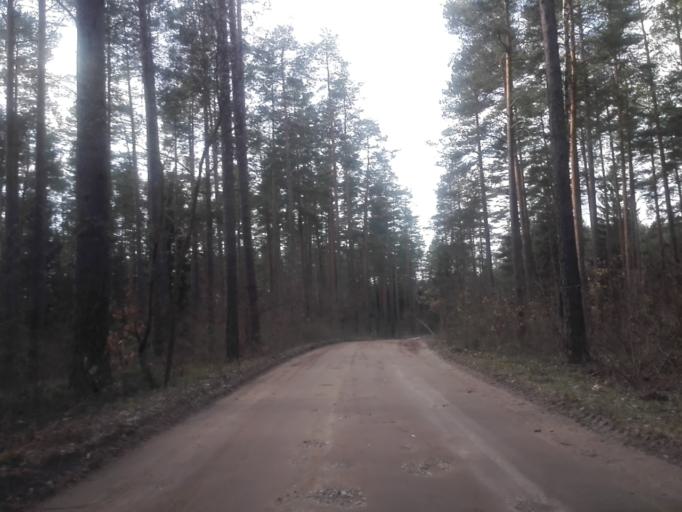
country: PL
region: Podlasie
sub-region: Powiat sejnenski
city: Sejny
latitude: 54.0237
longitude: 23.4081
